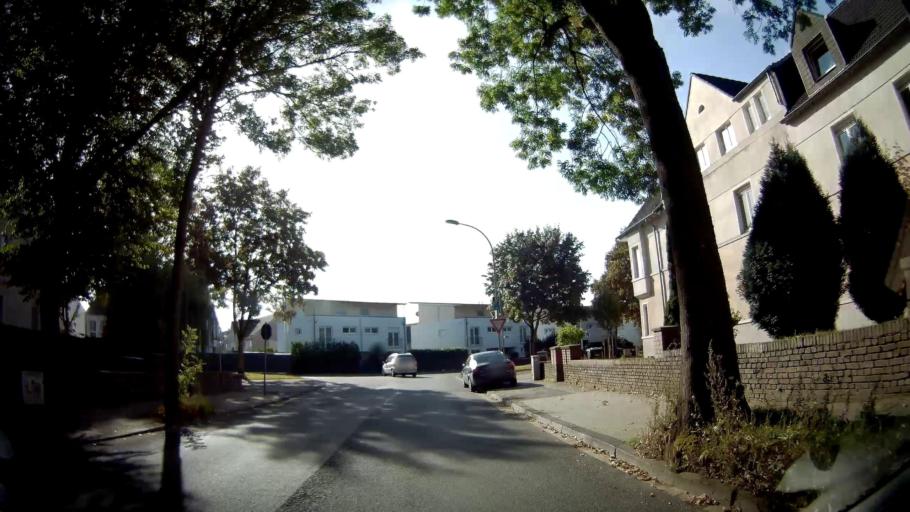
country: DE
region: North Rhine-Westphalia
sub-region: Regierungsbezirk Arnsberg
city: Herne
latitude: 51.5124
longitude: 7.2526
